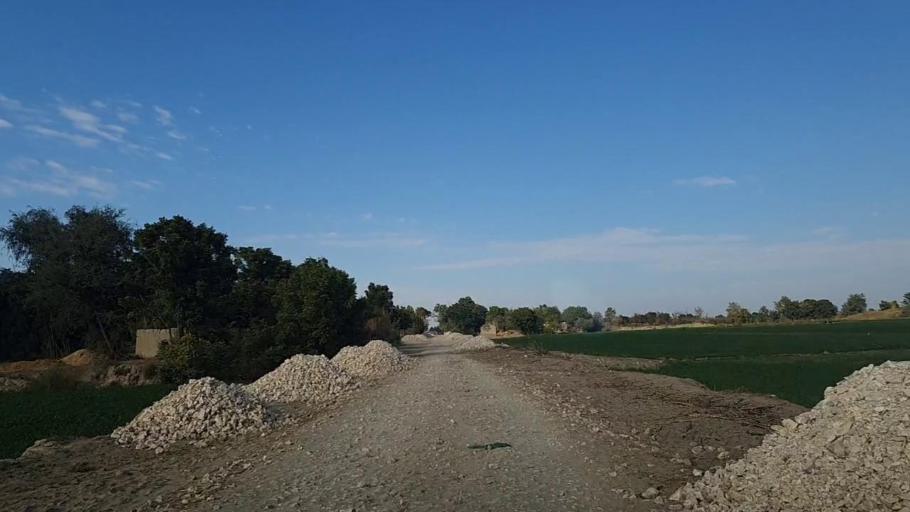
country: PK
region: Sindh
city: Jam Sahib
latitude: 26.3087
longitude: 68.8141
